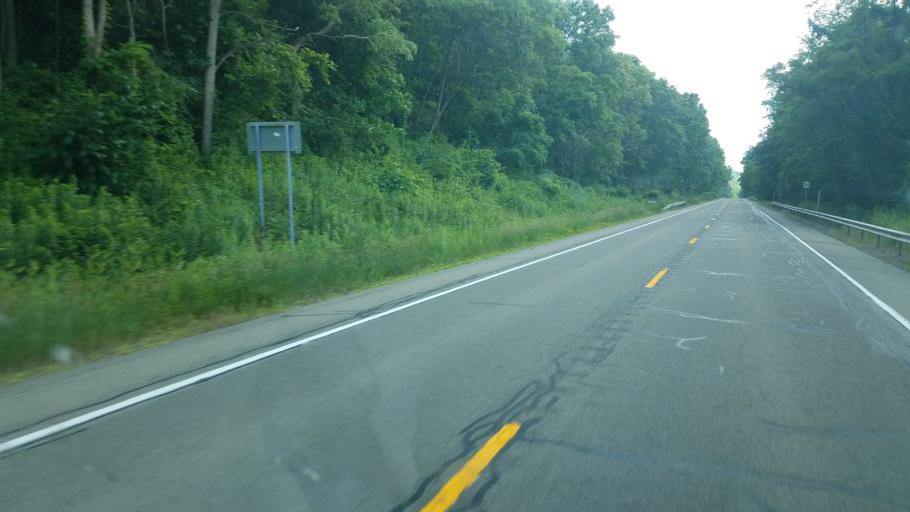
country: US
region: New York
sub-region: Steuben County
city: Sylvan Beach
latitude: 42.5323
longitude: -77.0998
